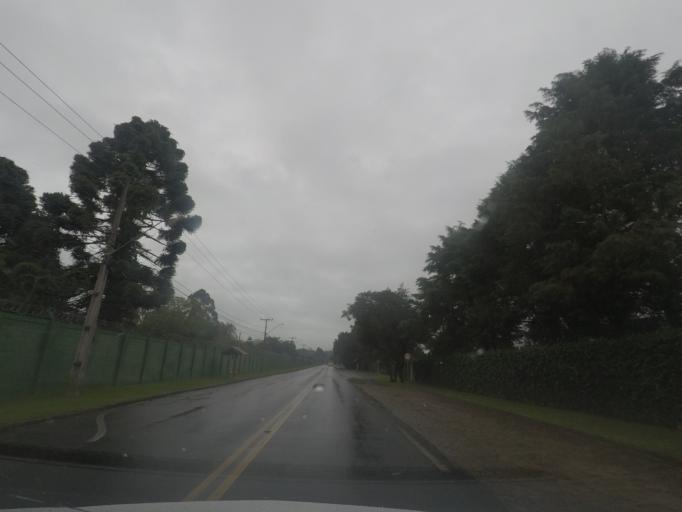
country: BR
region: Parana
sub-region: Quatro Barras
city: Quatro Barras
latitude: -25.3745
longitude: -49.0954
